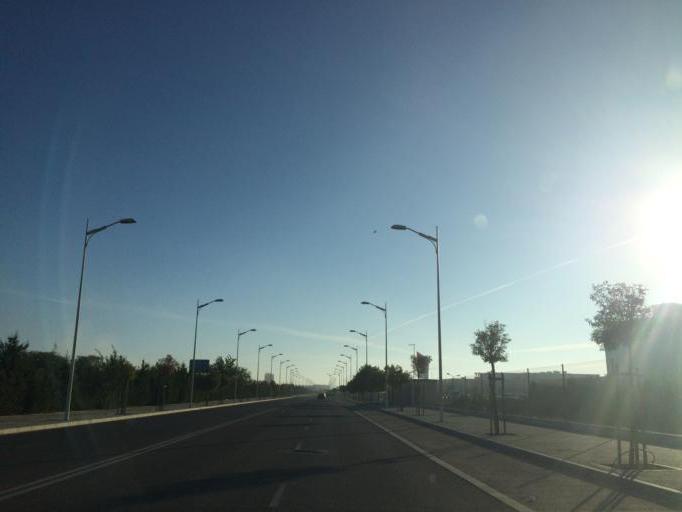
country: ES
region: Castille-La Mancha
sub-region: Provincia de Albacete
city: Albacete
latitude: 39.0079
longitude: -1.8850
